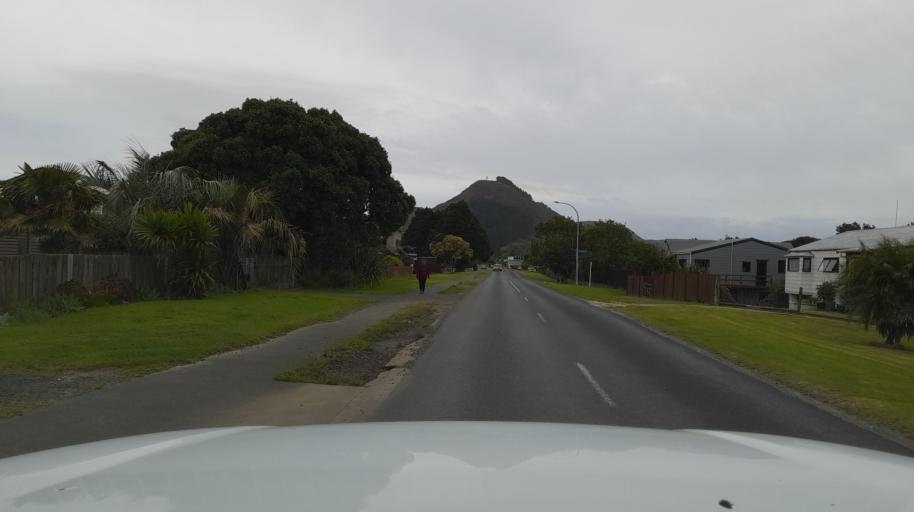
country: NZ
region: Northland
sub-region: Far North District
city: Ahipara
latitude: -35.1642
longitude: 173.1572
